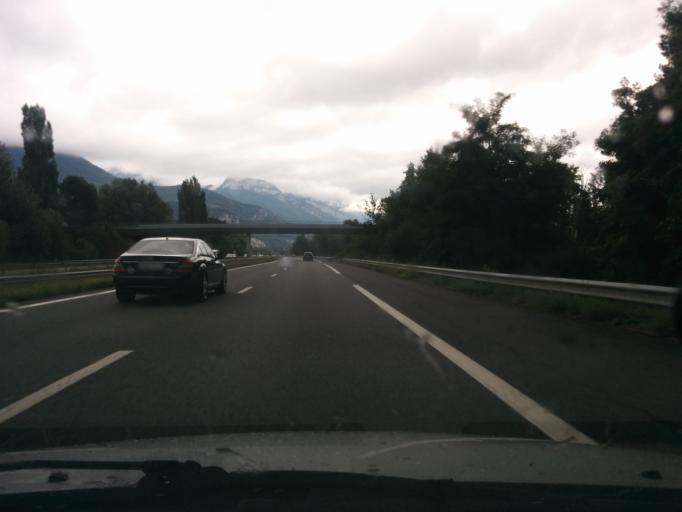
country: FR
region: Rhone-Alpes
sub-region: Departement de l'Isere
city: Saint-Jean-de-Moirans
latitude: 45.3294
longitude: 5.5924
